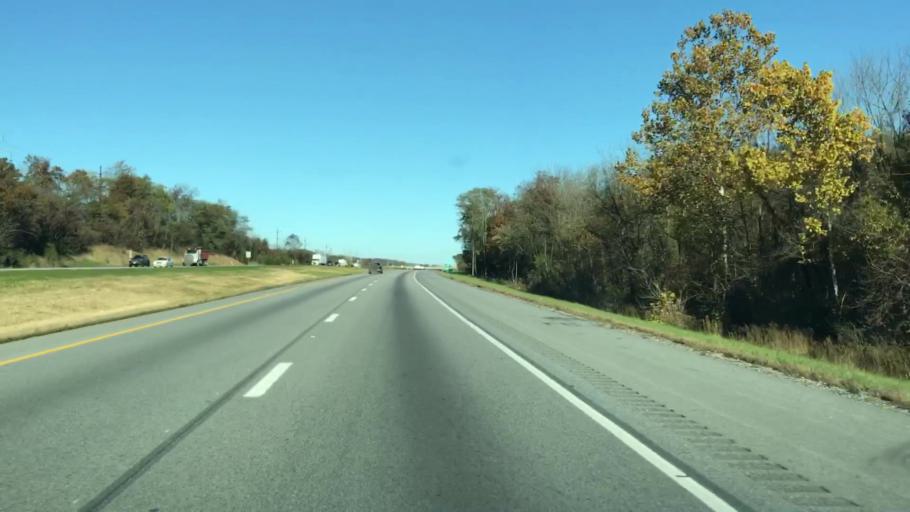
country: US
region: Pennsylvania
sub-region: Cumberland County
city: Mechanicsburg
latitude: 40.2622
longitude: -77.0568
